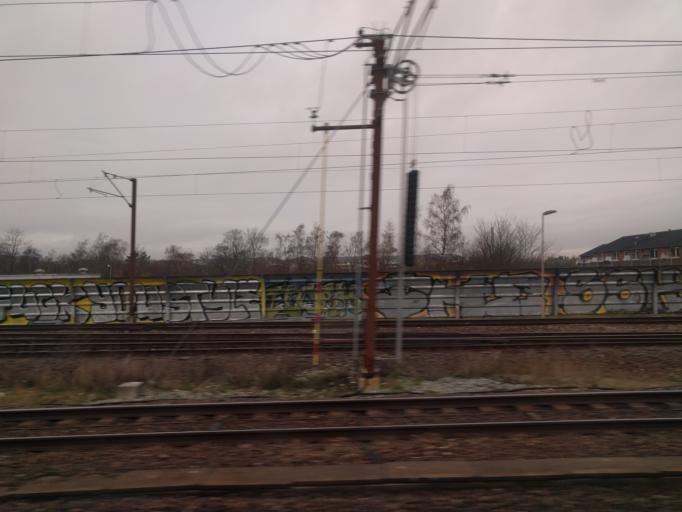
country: DK
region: Capital Region
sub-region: Hoje-Taastrup Kommune
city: Taastrup
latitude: 55.6515
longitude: 12.2927
